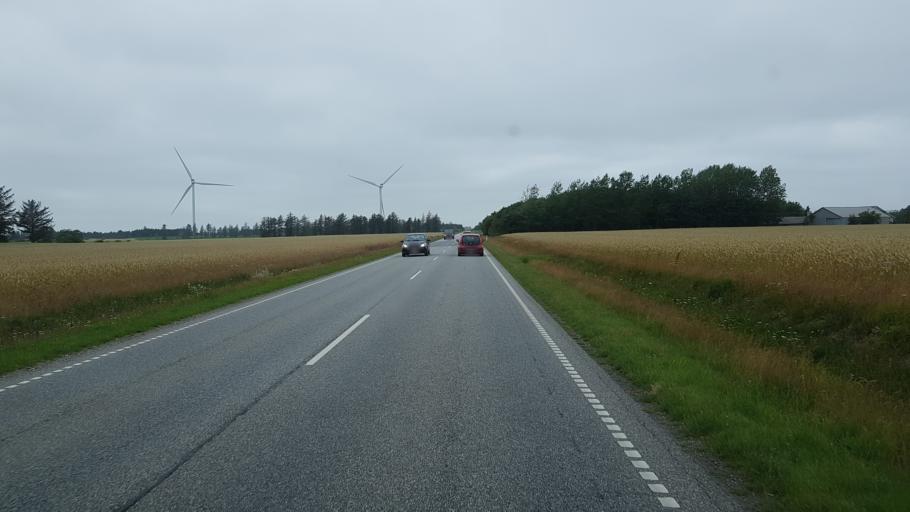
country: DK
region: Central Jutland
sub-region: Lemvig Kommune
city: Lemvig
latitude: 56.4423
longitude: 8.3635
